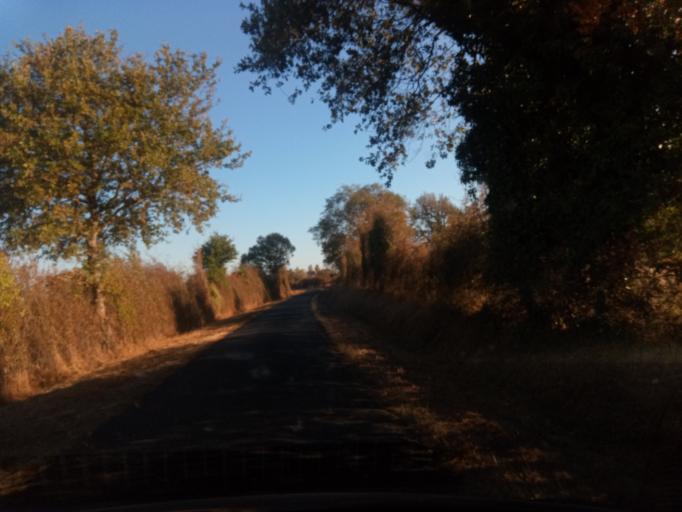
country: FR
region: Poitou-Charentes
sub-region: Departement de la Vienne
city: Saulge
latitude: 46.4043
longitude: 0.8692
